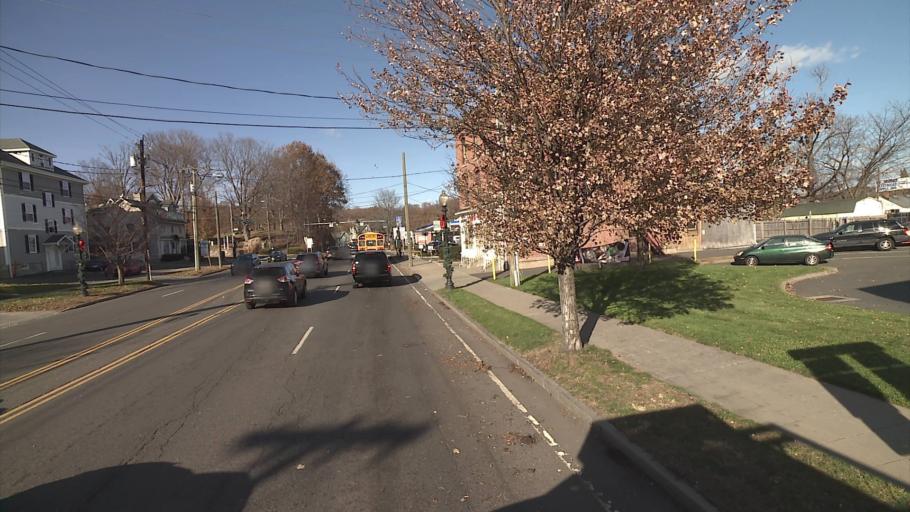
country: US
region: Connecticut
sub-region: Fairfield County
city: Danbury
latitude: 41.4029
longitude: -73.4592
